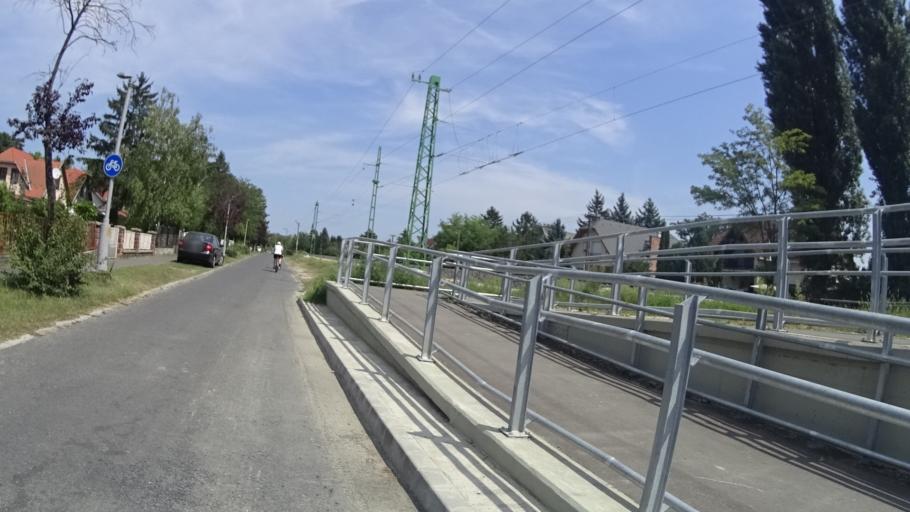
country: HU
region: Somogy
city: Fonyod
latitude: 46.7549
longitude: 17.5776
